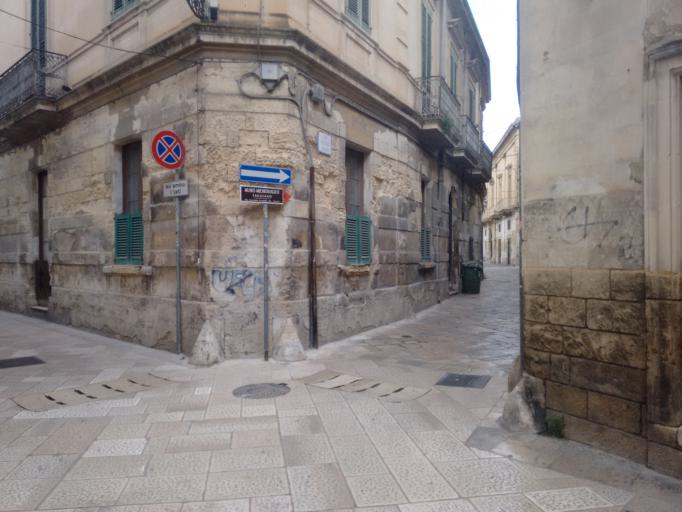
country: IT
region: Apulia
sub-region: Provincia di Lecce
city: Lecce
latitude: 40.3498
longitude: 18.1721
